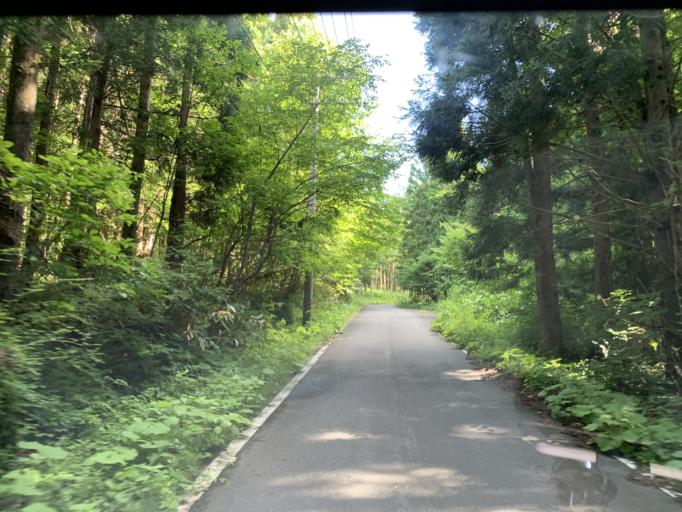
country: JP
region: Iwate
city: Ichinoseki
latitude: 38.8961
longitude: 140.9080
